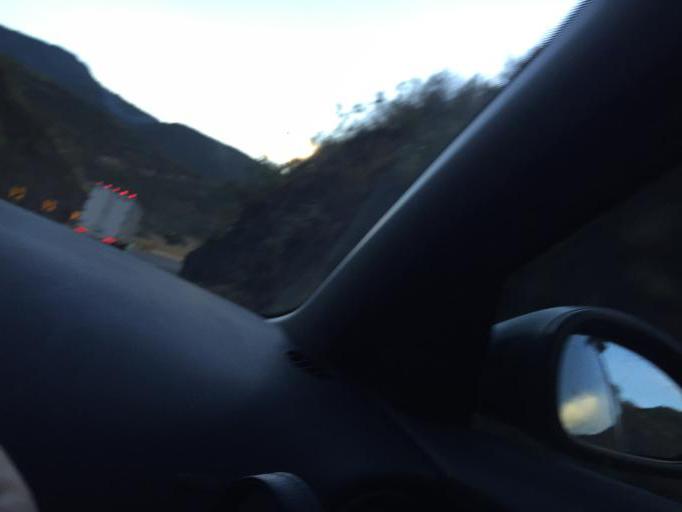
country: MX
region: Veracruz
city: Maltrata
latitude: 18.8230
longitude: -97.2381
